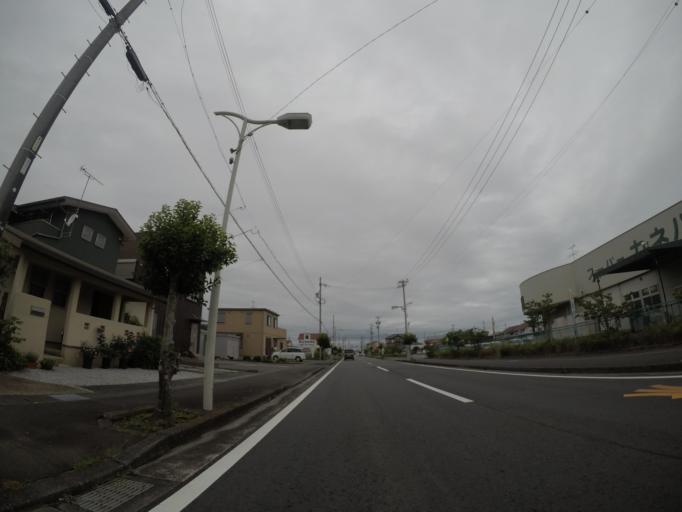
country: JP
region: Shizuoka
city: Sagara
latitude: 34.7475
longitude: 138.2290
